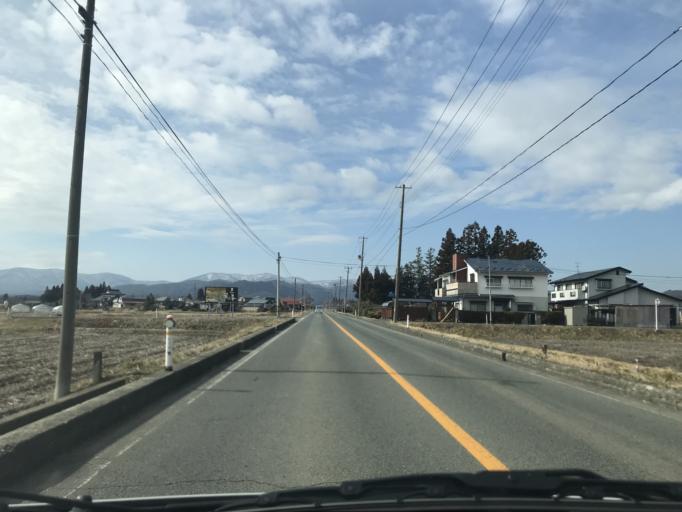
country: JP
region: Iwate
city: Hanamaki
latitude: 39.3852
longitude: 141.0660
